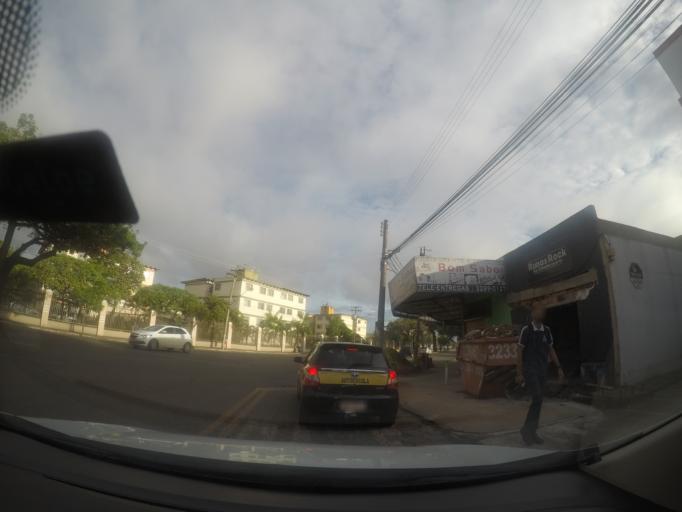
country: BR
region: Goias
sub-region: Goiania
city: Goiania
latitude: -16.6845
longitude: -49.3135
